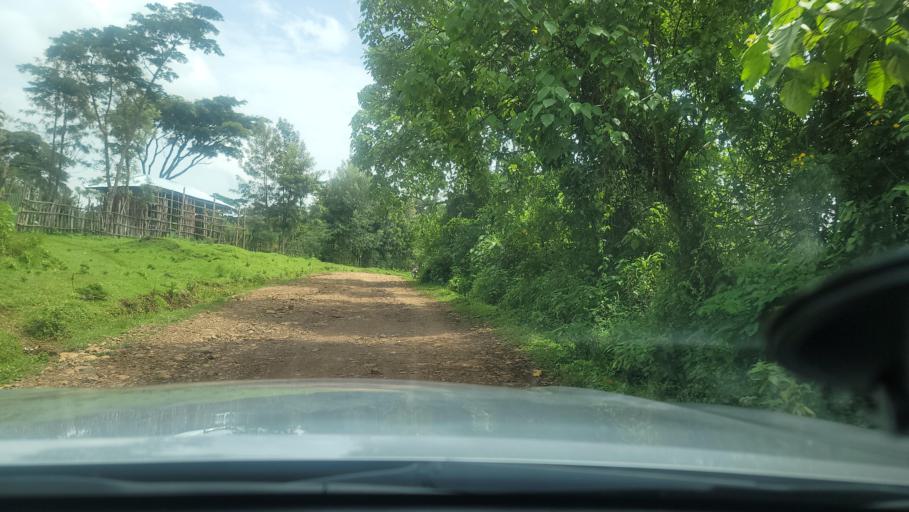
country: ET
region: Oromiya
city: Agaro
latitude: 7.8021
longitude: 36.4171
